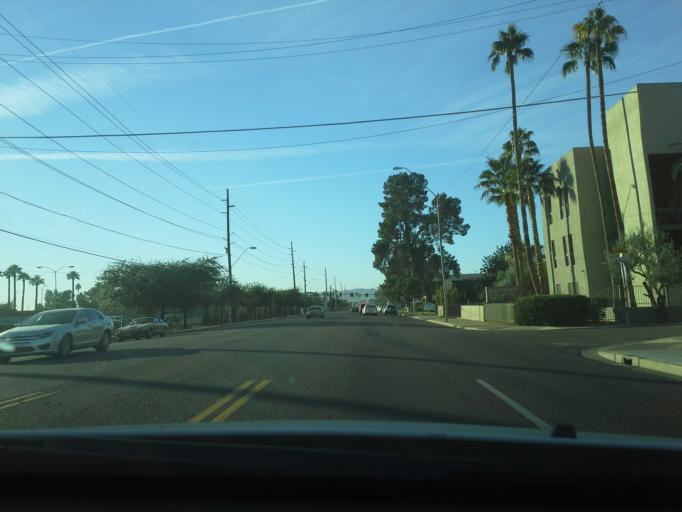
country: US
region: Arizona
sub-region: Maricopa County
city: Phoenix
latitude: 33.4823
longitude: -112.0651
